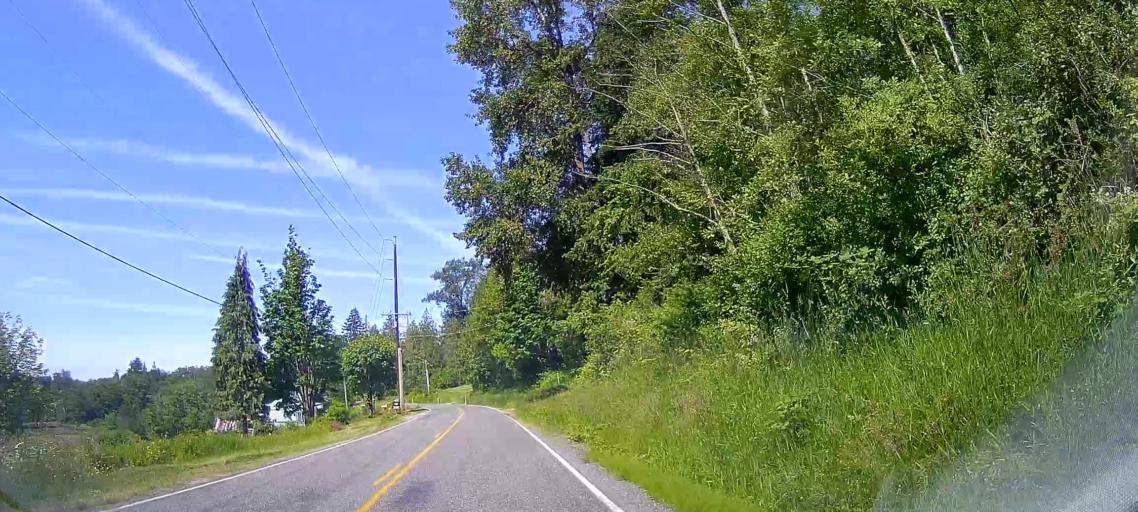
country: US
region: Washington
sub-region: Skagit County
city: Burlington
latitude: 48.5349
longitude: -122.2956
